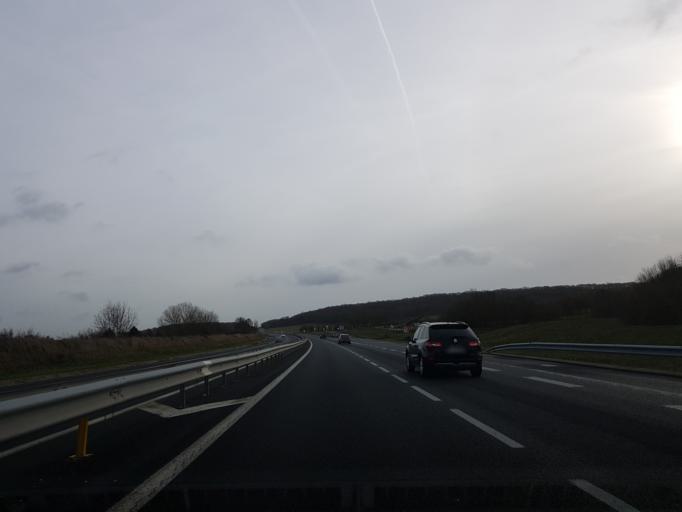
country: FR
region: Bourgogne
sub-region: Departement de l'Yonne
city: Soucy
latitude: 48.2480
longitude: 3.3455
